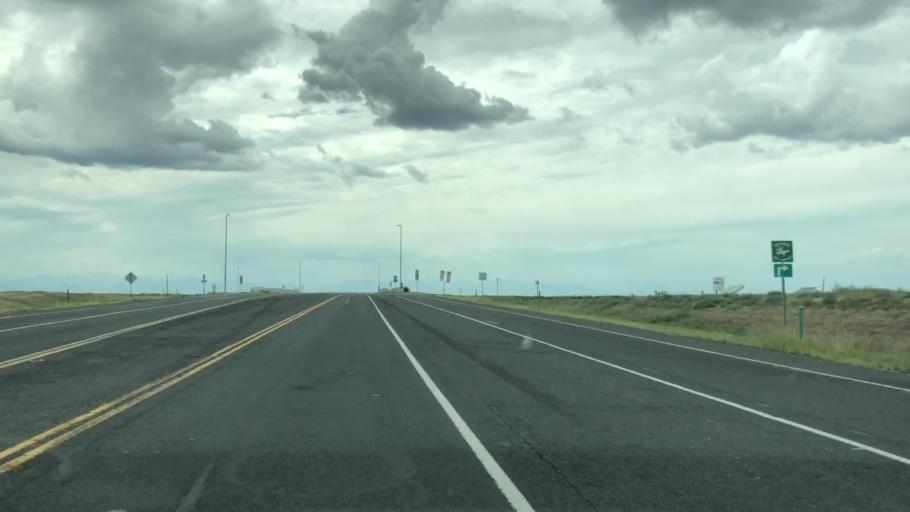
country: US
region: Colorado
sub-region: Adams County
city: Aurora
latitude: 39.7980
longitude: -104.7141
